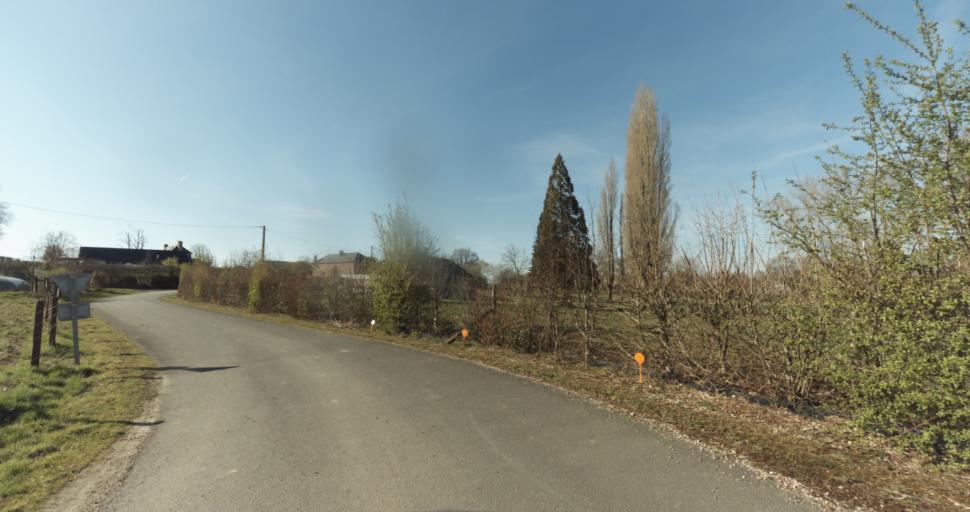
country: FR
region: Lower Normandy
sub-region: Departement du Calvados
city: Livarot
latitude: 49.0195
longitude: 0.0646
